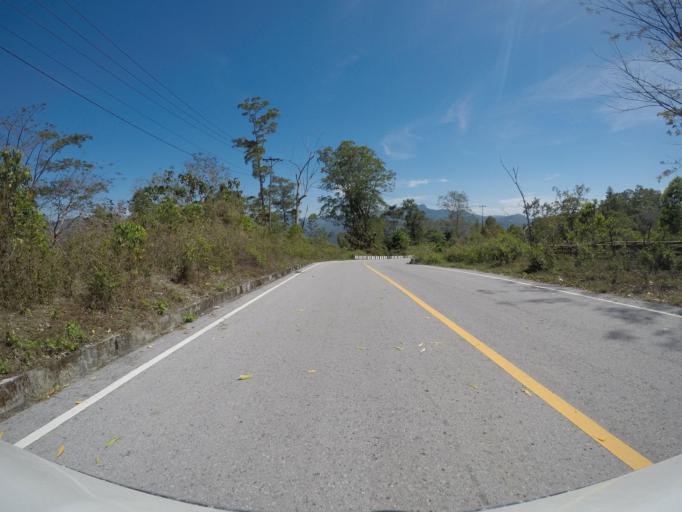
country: TL
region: Manufahi
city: Same
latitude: -8.8918
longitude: 125.9830
